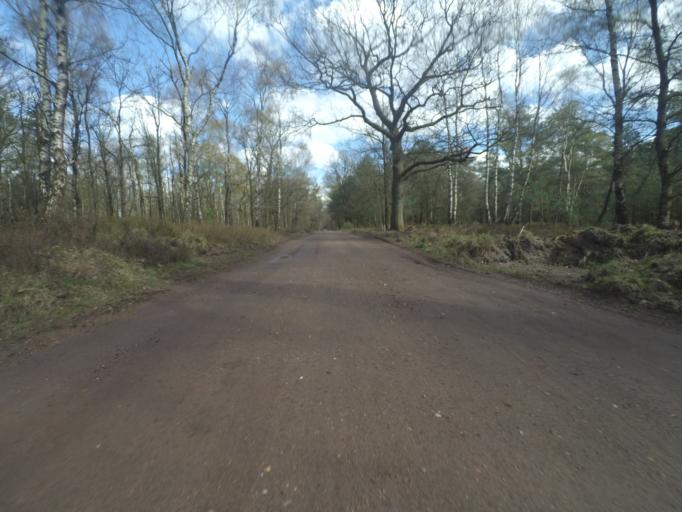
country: NL
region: Gelderland
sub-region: Gemeente Rozendaal
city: Rozendaal
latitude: 52.0827
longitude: 5.9432
